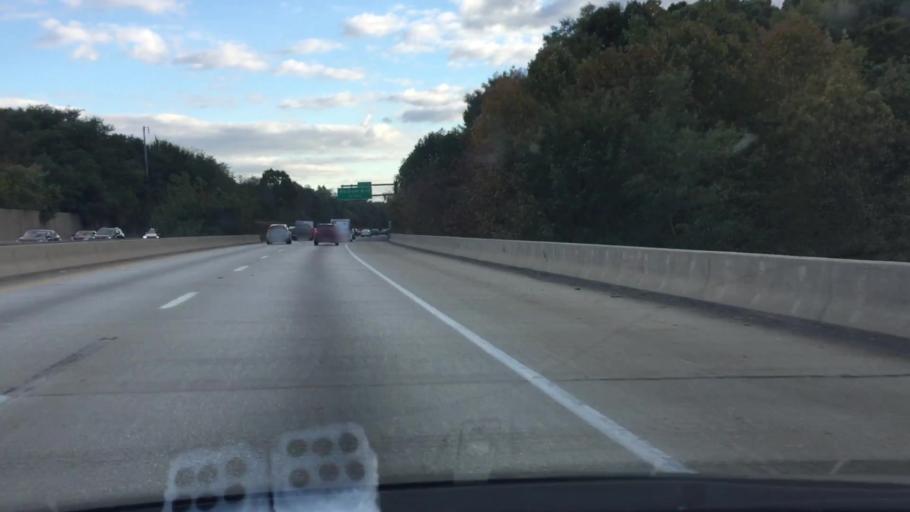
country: US
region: Pennsylvania
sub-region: Delaware County
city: Swarthmore
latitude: 39.8843
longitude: -75.3533
